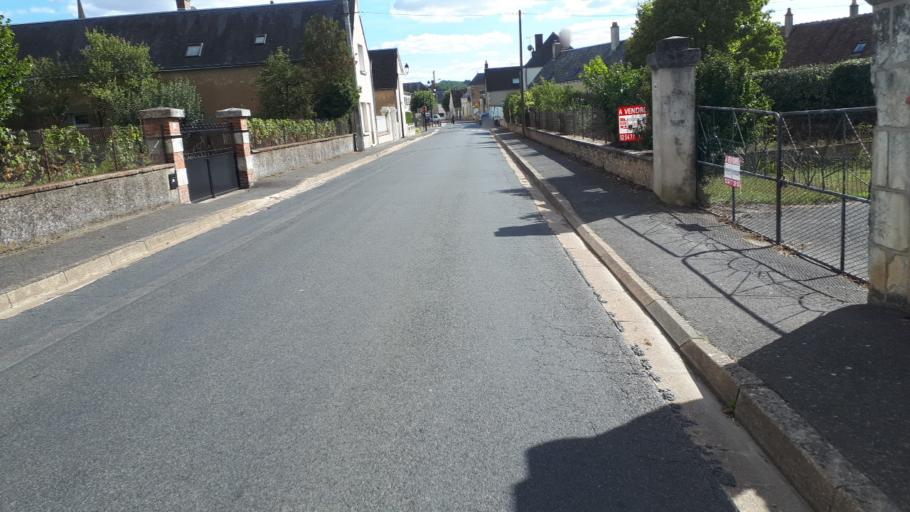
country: FR
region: Centre
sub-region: Departement du Loir-et-Cher
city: Villiers-sur-Loir
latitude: 47.7901
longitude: 0.9627
